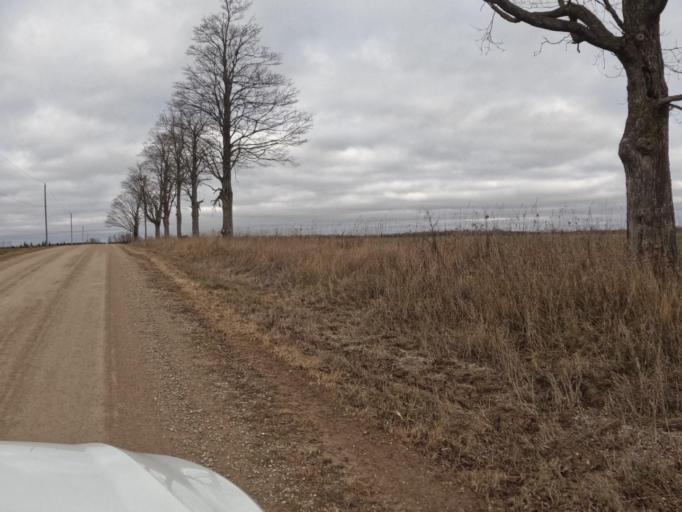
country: CA
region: Ontario
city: Shelburne
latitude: 43.8913
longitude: -80.4066
